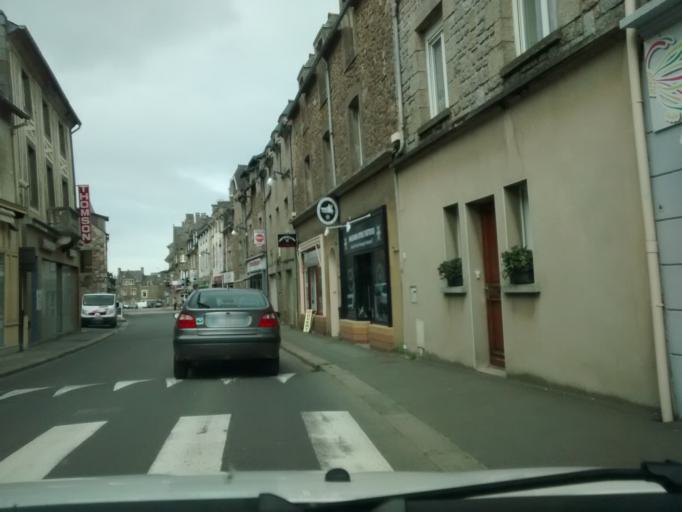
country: FR
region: Brittany
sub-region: Departement d'Ille-et-Vilaine
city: Pleurtuit
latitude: 48.5786
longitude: -2.0587
